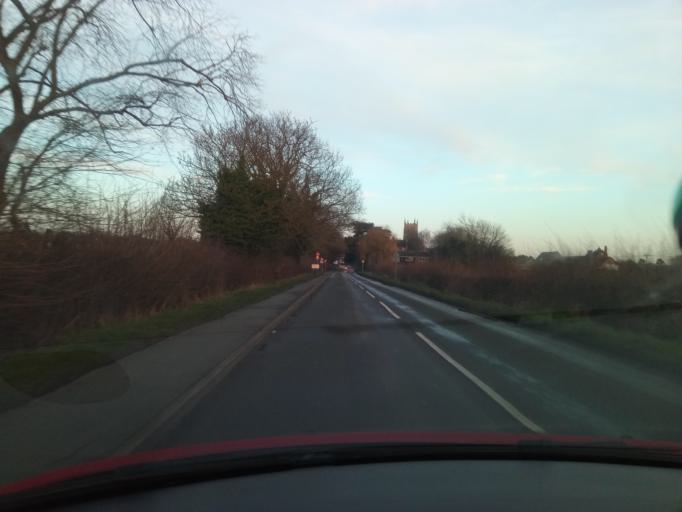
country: GB
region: England
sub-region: Leicestershire
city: Sileby
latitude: 52.7299
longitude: -1.1169
